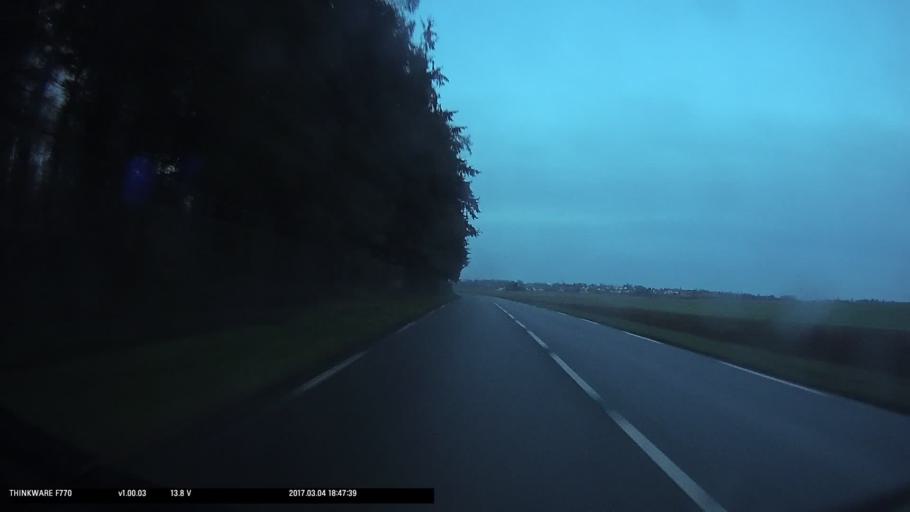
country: FR
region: Ile-de-France
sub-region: Departement du Val-d'Oise
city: Us
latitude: 49.1121
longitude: 1.9795
